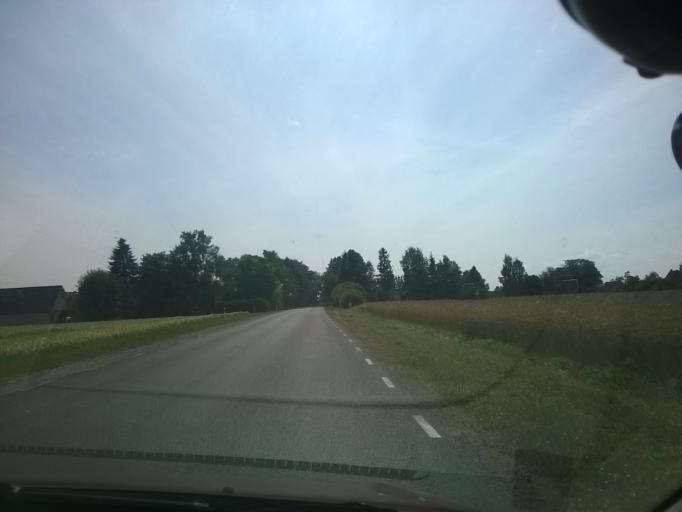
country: EE
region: Tartu
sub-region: Puhja vald
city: Puhja
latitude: 58.2845
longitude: 26.1755
